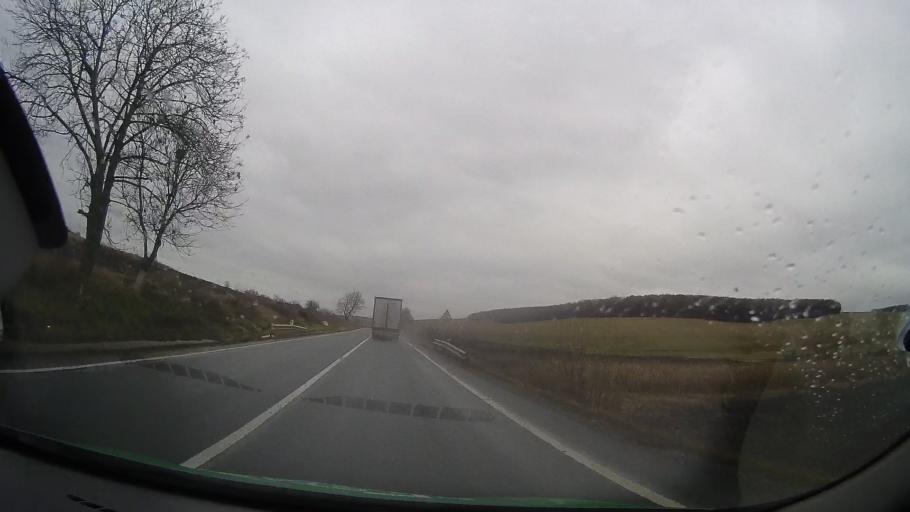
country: RO
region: Mures
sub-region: Comuna Lunca
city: Lunca
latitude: 46.8612
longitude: 24.5554
